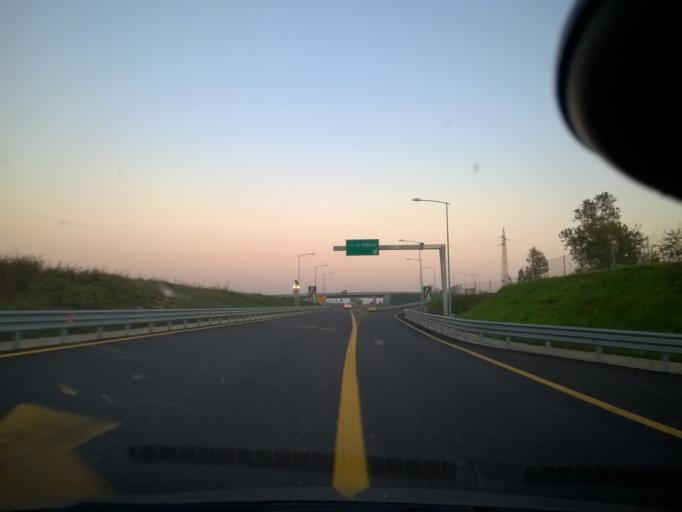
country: IT
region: Lombardy
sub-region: Provincia di Brescia
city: Travagliato
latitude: 45.5287
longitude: 10.0519
